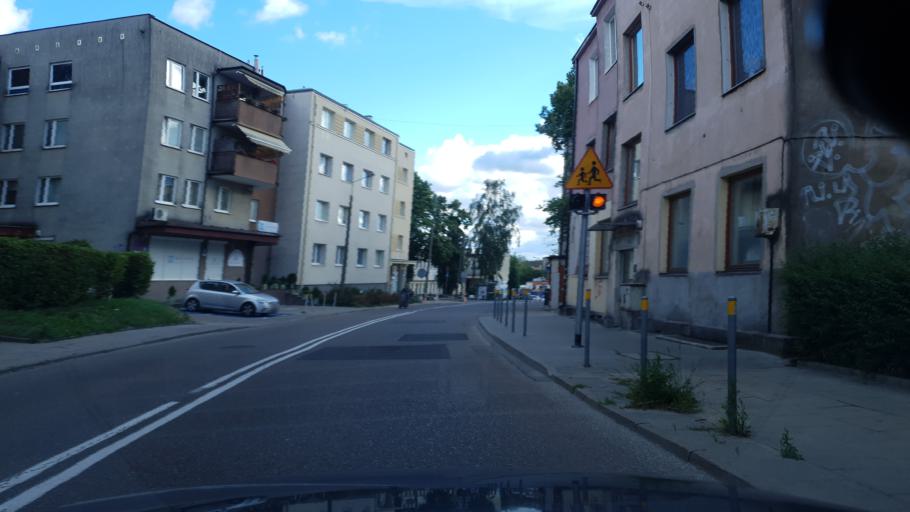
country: PL
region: Pomeranian Voivodeship
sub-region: Gdynia
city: Gdynia
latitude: 54.5041
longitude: 18.5428
